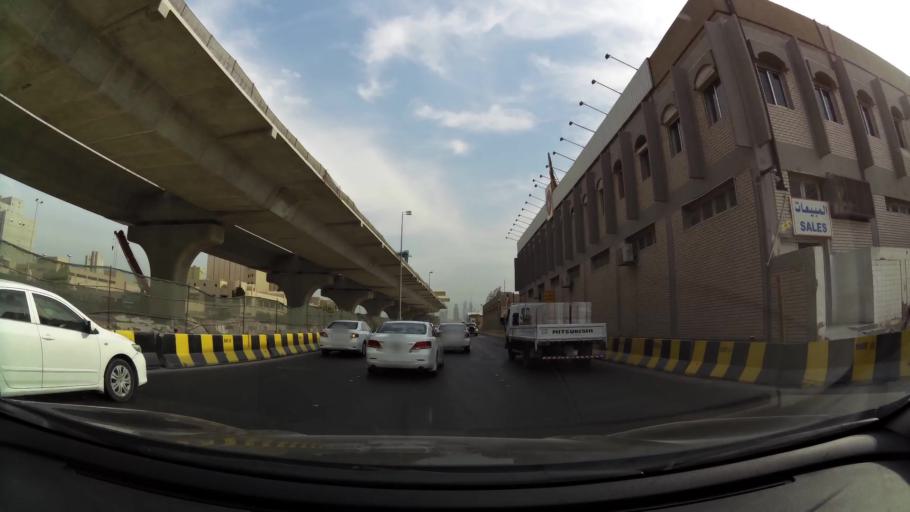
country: KW
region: Al Asimah
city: Ash Shamiyah
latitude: 29.3462
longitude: 47.9363
